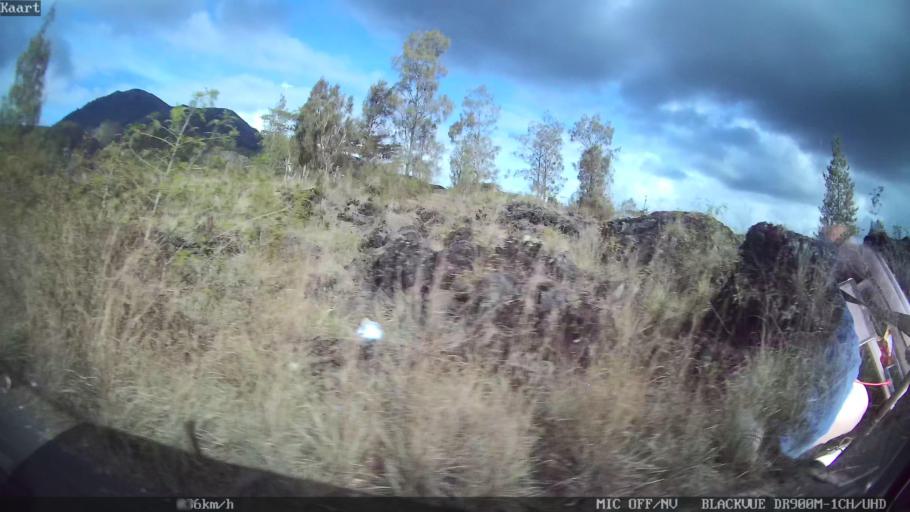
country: ID
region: Bali
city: Banjar Kedisan
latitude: -8.2379
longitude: 115.3536
